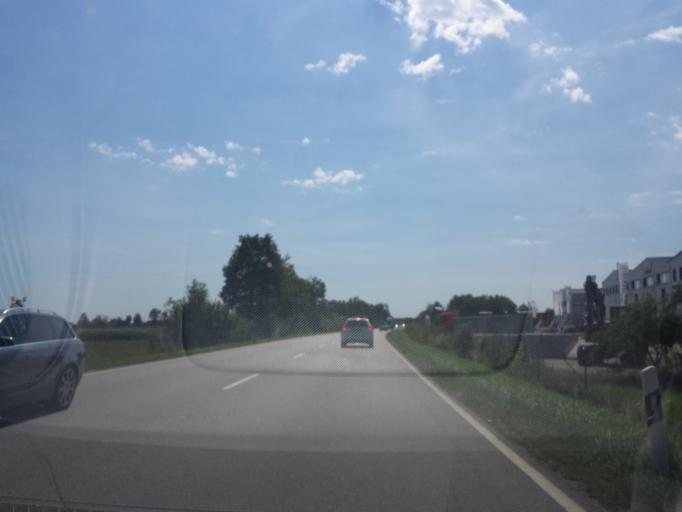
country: DE
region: Bavaria
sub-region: Lower Bavaria
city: Steinach
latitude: 48.9545
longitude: 12.6230
